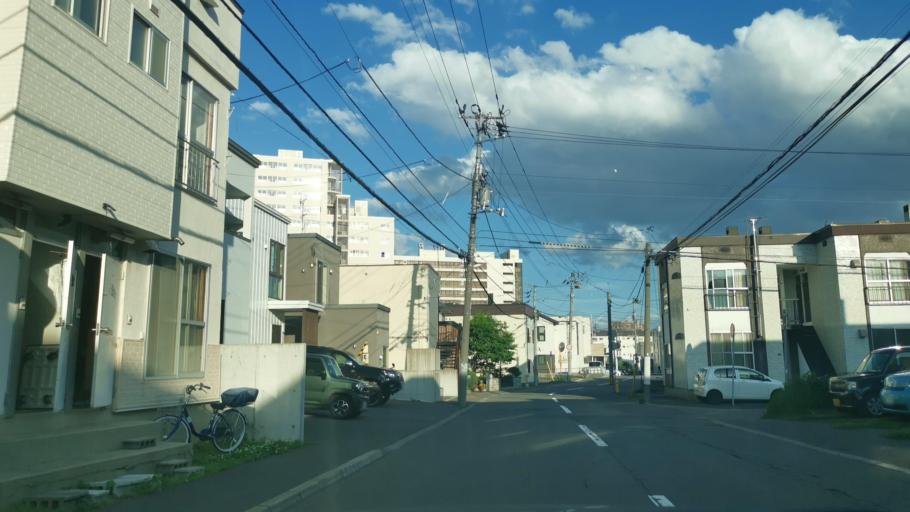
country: JP
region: Hokkaido
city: Sapporo
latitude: 43.0691
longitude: 141.3132
